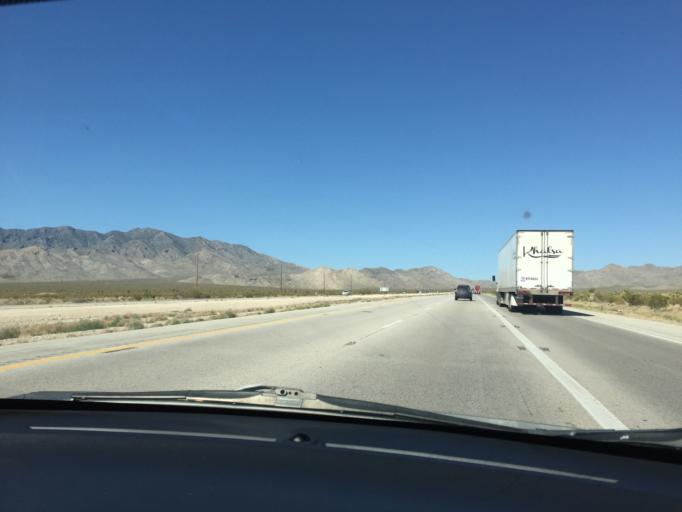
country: US
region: Nevada
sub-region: Clark County
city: Sandy Valley
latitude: 35.4518
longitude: -115.6519
